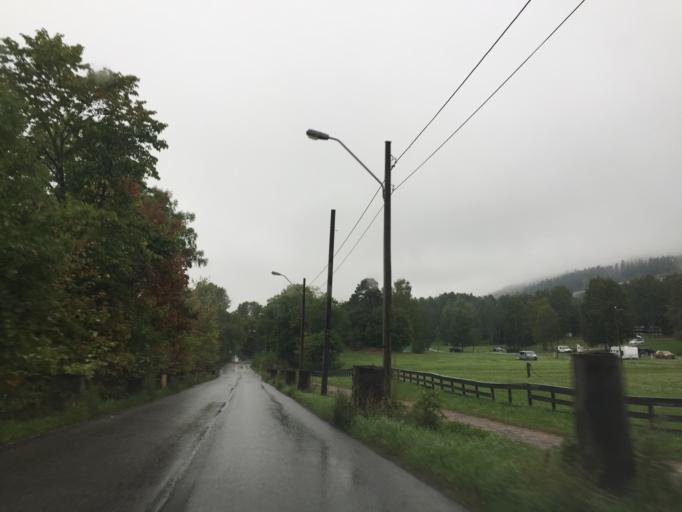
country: NO
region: Akershus
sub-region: Baerum
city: Lysaker
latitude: 59.9630
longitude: 10.6399
